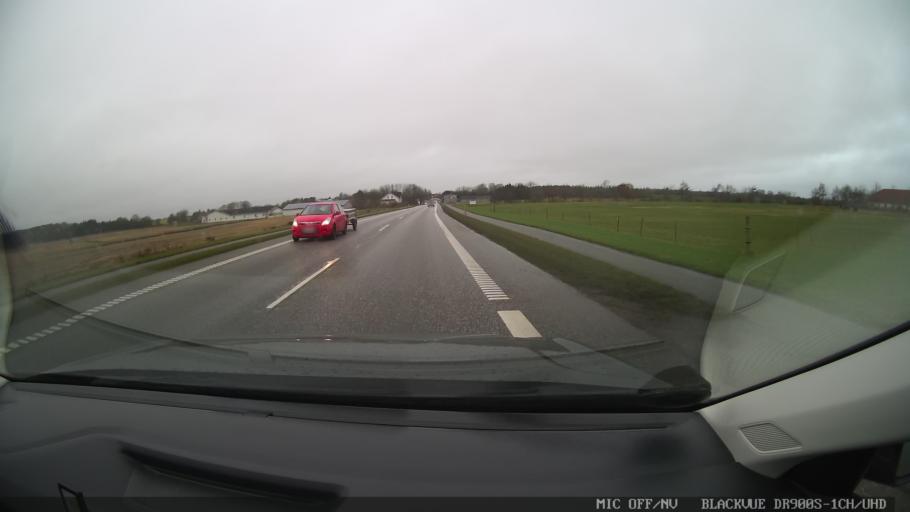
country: DK
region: Central Jutland
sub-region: Viborg Kommune
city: Karup
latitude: 56.3270
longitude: 9.2641
